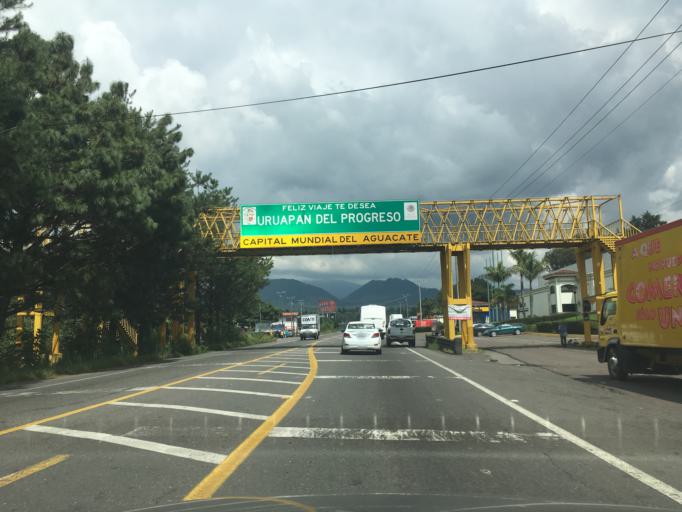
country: MX
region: Michoacan
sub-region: Uruapan
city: Uruapan
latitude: 19.4733
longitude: -102.0727
